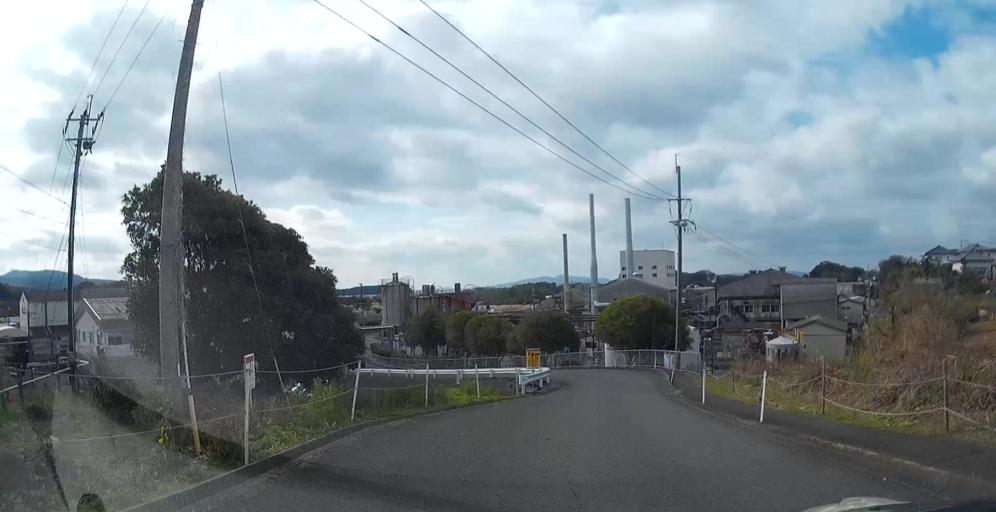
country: JP
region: Kumamoto
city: Minamata
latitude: 32.2041
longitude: 130.3817
